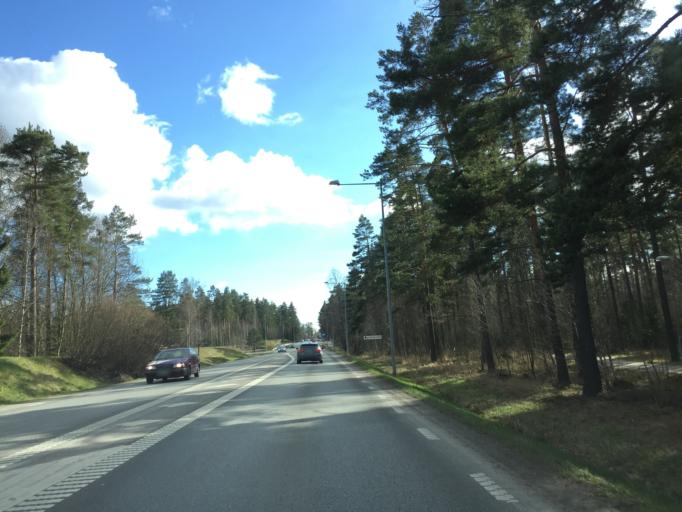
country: SE
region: OErebro
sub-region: Kumla Kommun
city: Kumla
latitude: 59.1484
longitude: 15.1407
